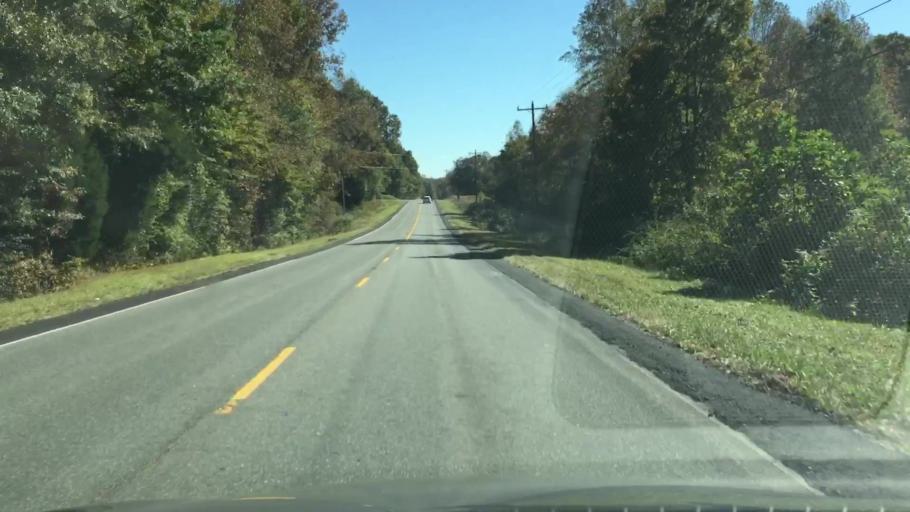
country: US
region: North Carolina
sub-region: Rockingham County
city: Reidsville
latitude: 36.2857
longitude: -79.6548
